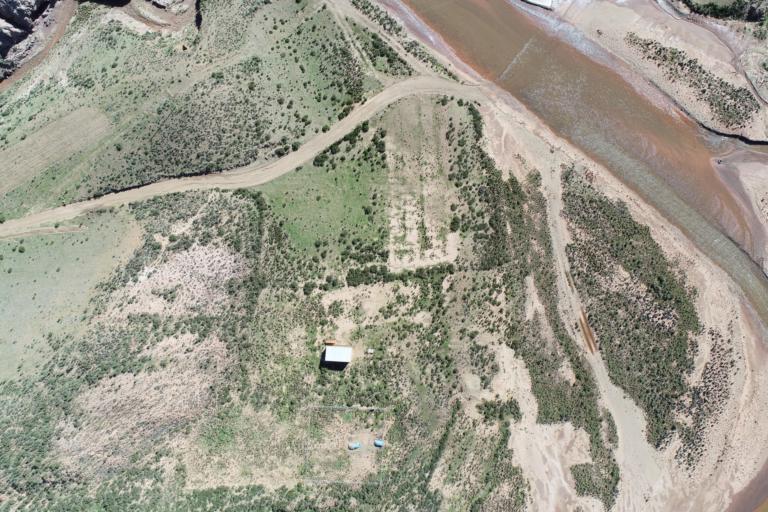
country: BO
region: La Paz
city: Curahuara de Carangas
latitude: -17.3022
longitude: -68.4886
